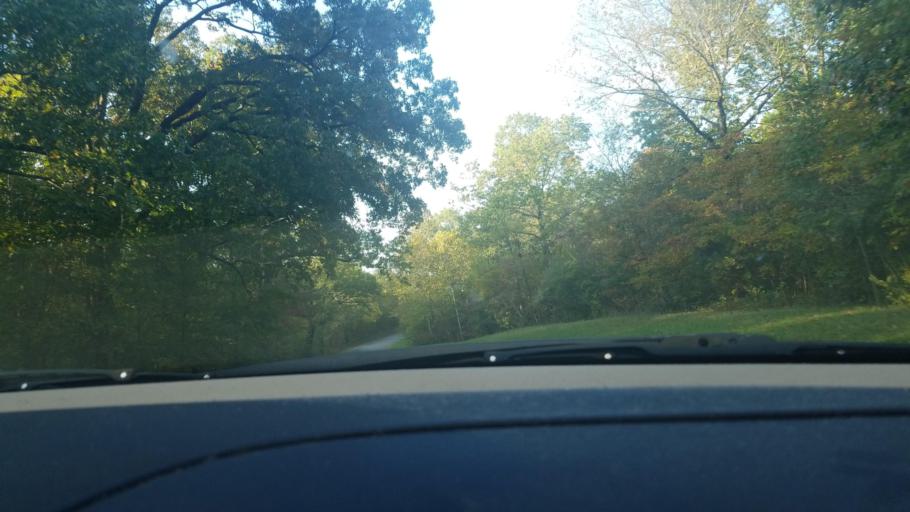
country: US
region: Illinois
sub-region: Saline County
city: Carrier Mills
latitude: 37.7740
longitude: -88.7143
